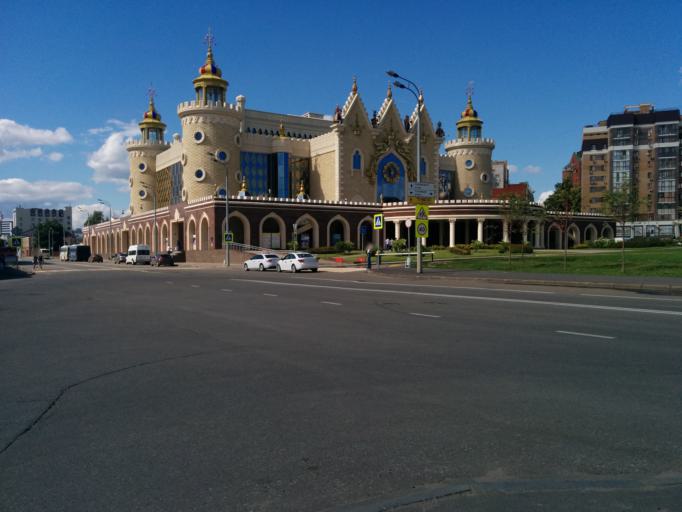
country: RU
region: Tatarstan
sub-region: Gorod Kazan'
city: Kazan
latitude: 55.7787
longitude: 49.1388
